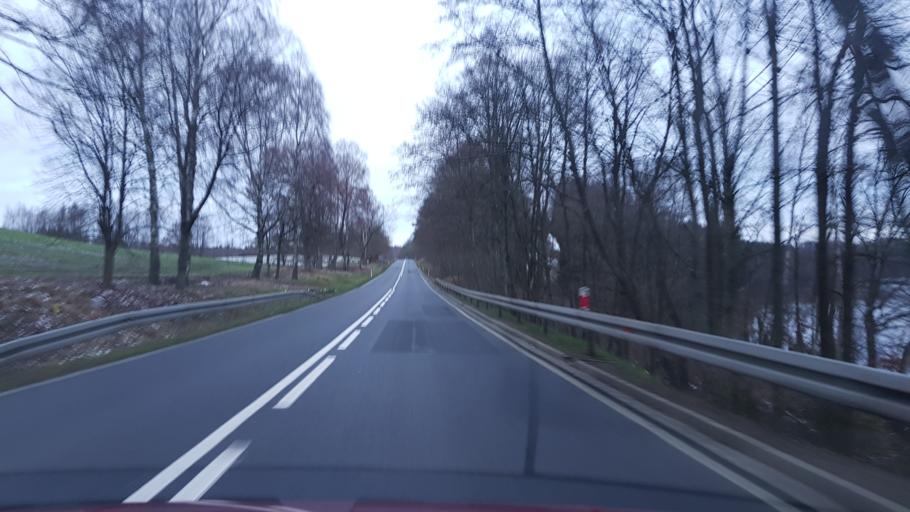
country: PL
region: Pomeranian Voivodeship
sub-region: Powiat czluchowski
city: Koczala
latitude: 54.0137
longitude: 17.1175
